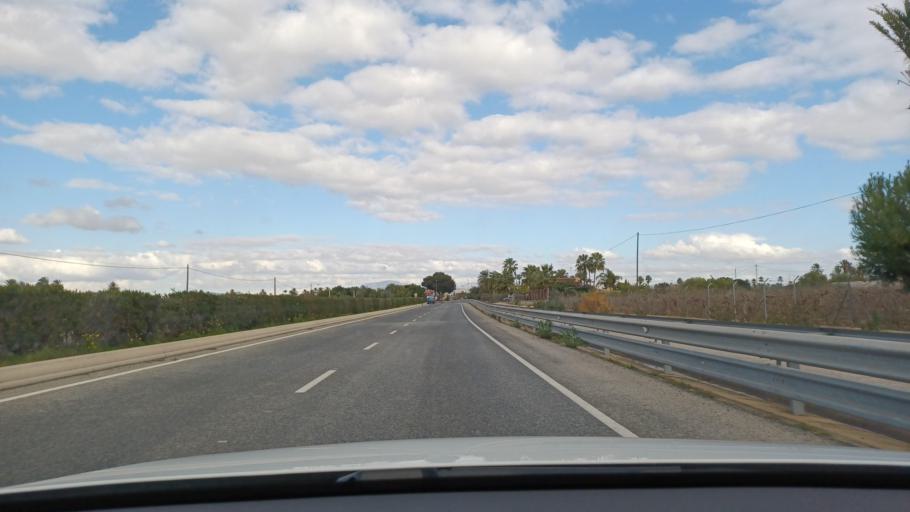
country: ES
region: Valencia
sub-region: Provincia de Alicante
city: Elche
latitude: 38.2107
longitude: -0.6975
